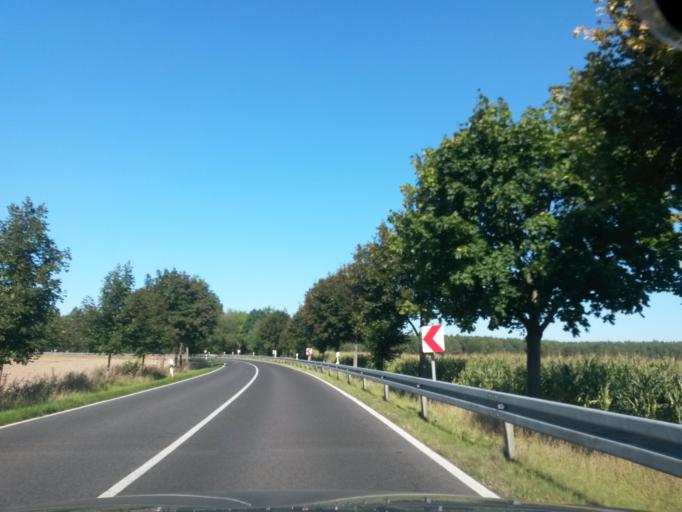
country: DE
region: Brandenburg
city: Templin
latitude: 53.1491
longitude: 13.4511
